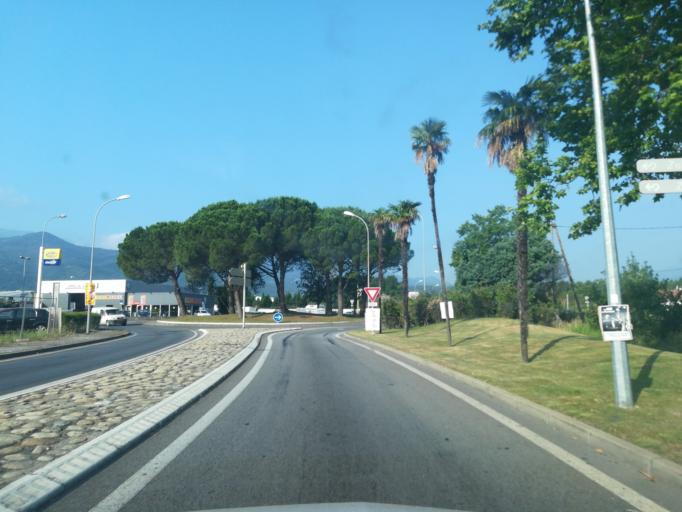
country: FR
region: Languedoc-Roussillon
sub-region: Departement des Pyrenees-Orientales
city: Ceret
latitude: 42.5026
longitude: 2.7596
